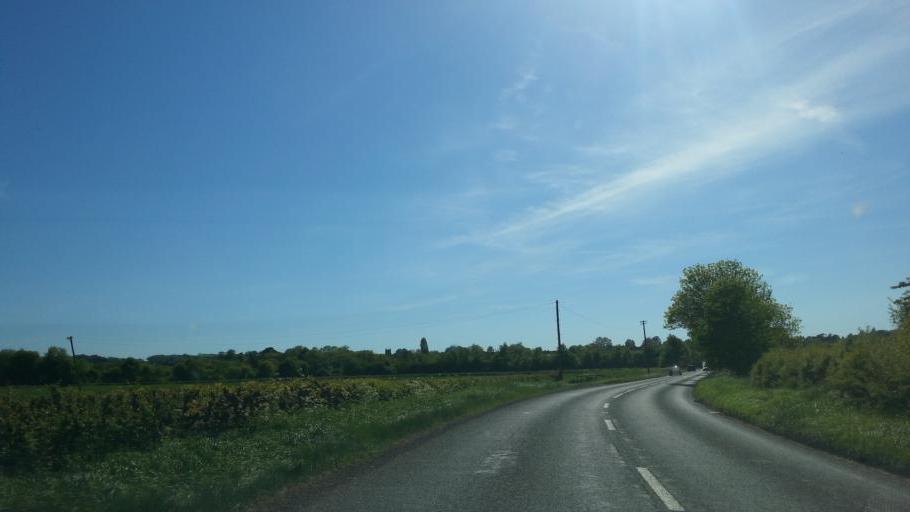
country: GB
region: England
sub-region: Dorset
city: Stalbridge
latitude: 50.9832
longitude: -2.3861
